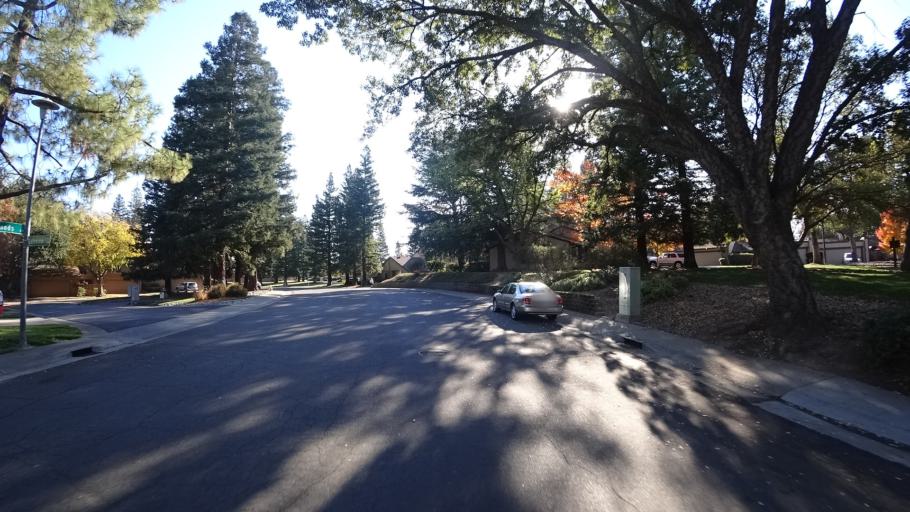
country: US
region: California
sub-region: Sacramento County
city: Citrus Heights
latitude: 38.6818
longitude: -121.3015
